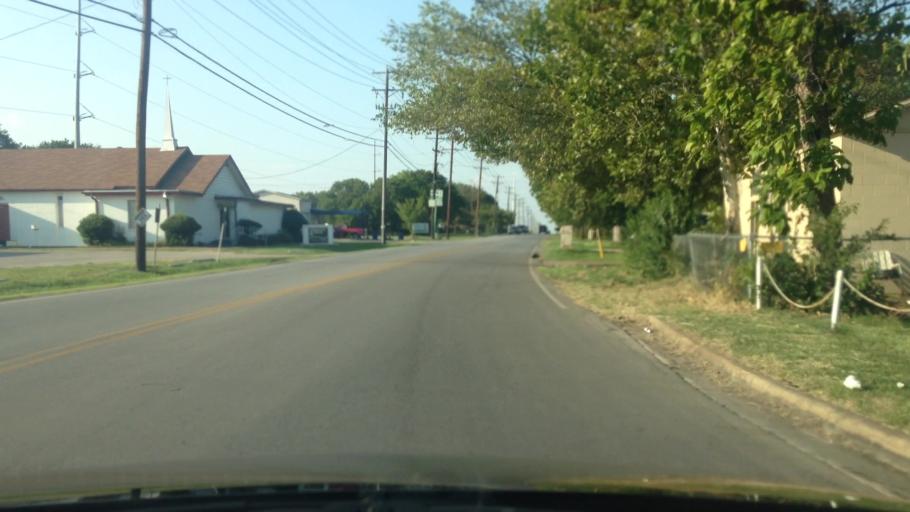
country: US
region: Texas
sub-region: Tarrant County
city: Everman
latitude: 32.6384
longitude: -97.2874
